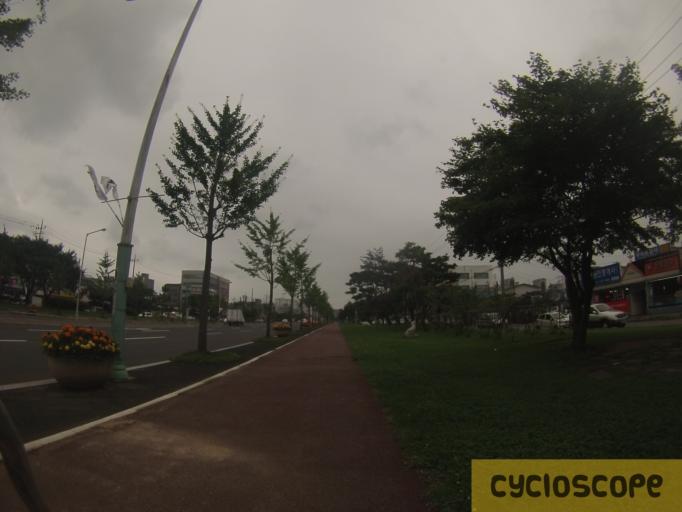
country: KR
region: Chungcheongnam-do
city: Taisen-ri
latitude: 36.4208
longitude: 126.7106
